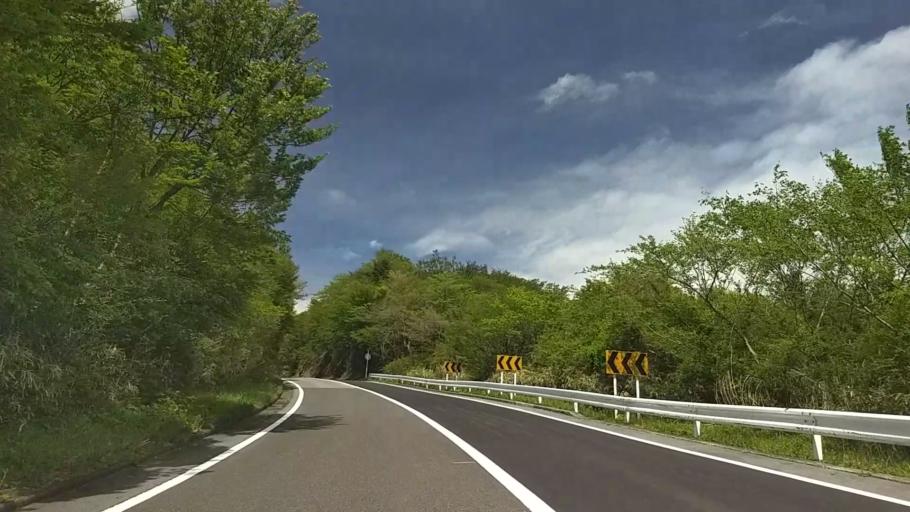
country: JP
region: Kanagawa
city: Hakone
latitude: 35.1932
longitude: 139.0649
